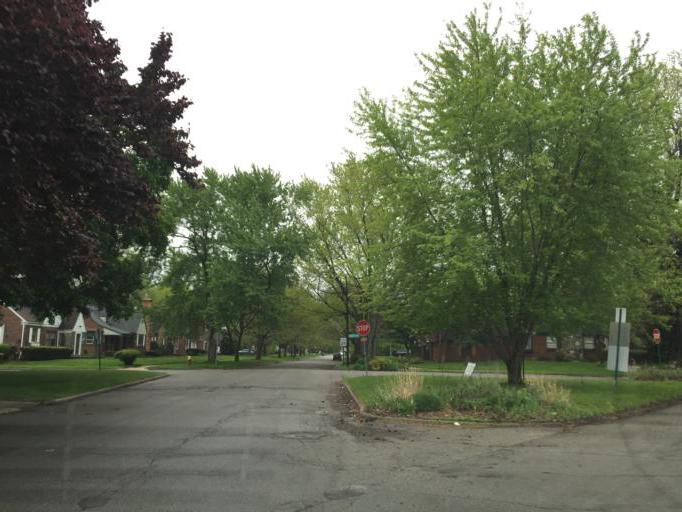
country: US
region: Michigan
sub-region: Wayne County
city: Redford
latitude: 42.3987
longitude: -83.2325
